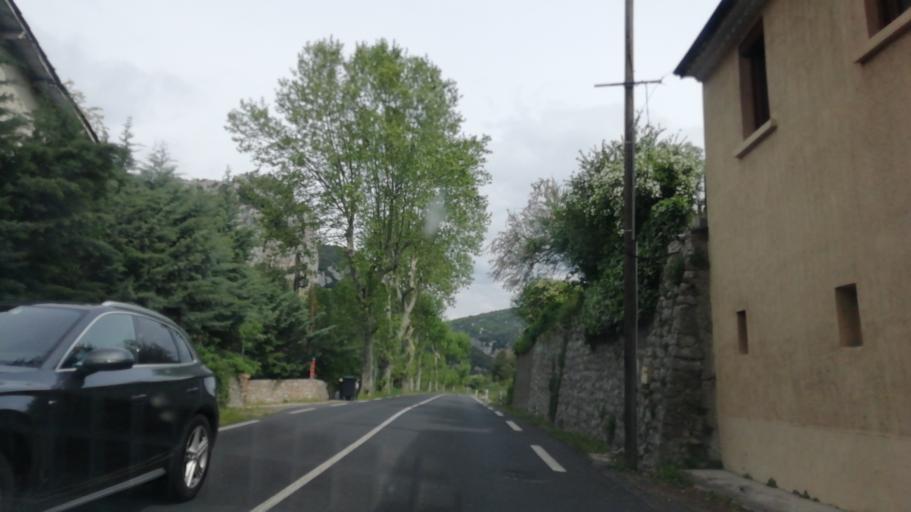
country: FR
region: Languedoc-Roussillon
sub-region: Departement de l'Herault
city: Saint-Bauzille-de-Putois
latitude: 43.9049
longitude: 3.7378
